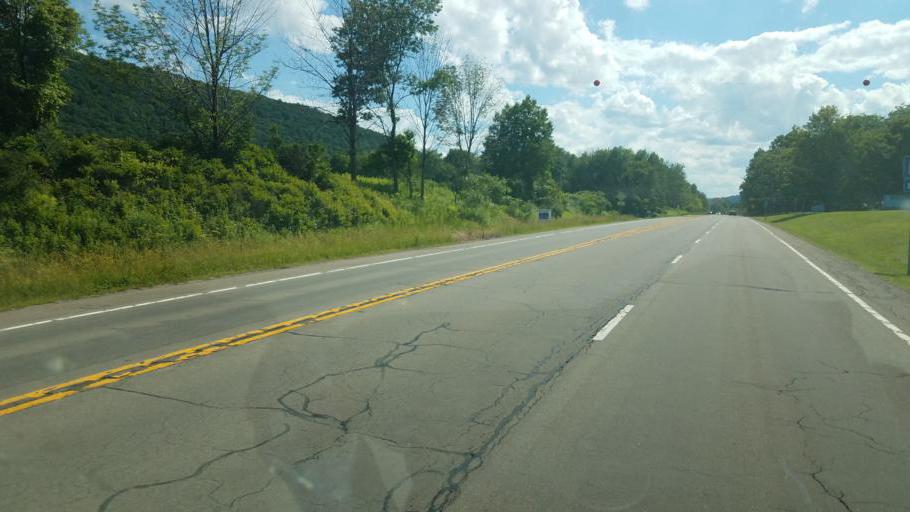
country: US
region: New York
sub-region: Steuben County
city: Bath
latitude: 42.3740
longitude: -77.2767
